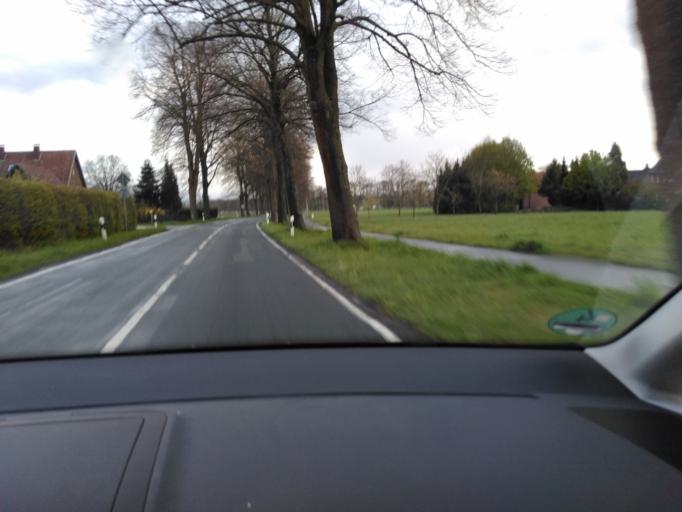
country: DE
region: North Rhine-Westphalia
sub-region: Regierungsbezirk Detmold
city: Verl
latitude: 51.9003
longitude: 8.5011
